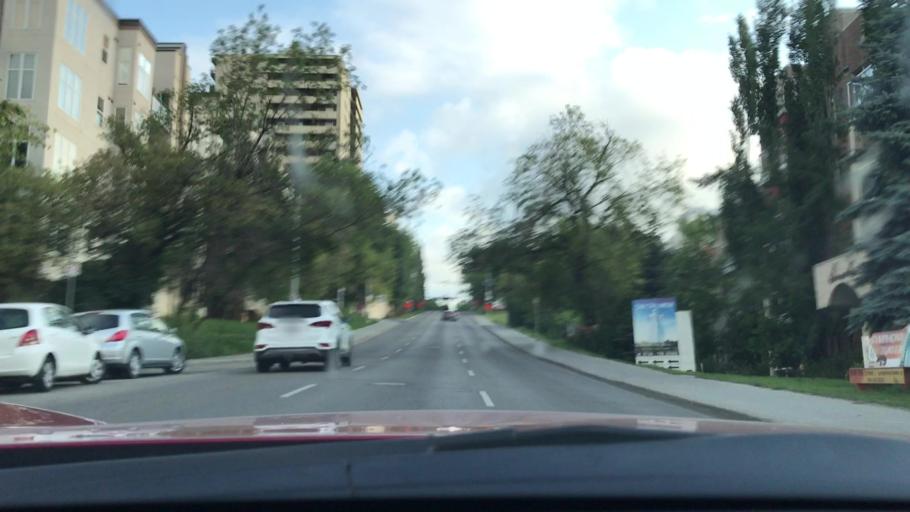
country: CA
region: Alberta
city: Edmonton
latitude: 53.5347
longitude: -113.5011
